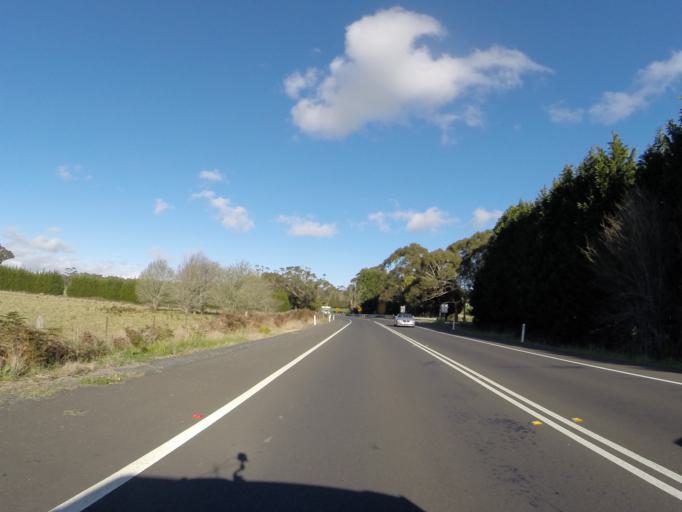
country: AU
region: New South Wales
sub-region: Wingecarribee
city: Moss Vale
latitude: -34.5789
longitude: 150.4934
